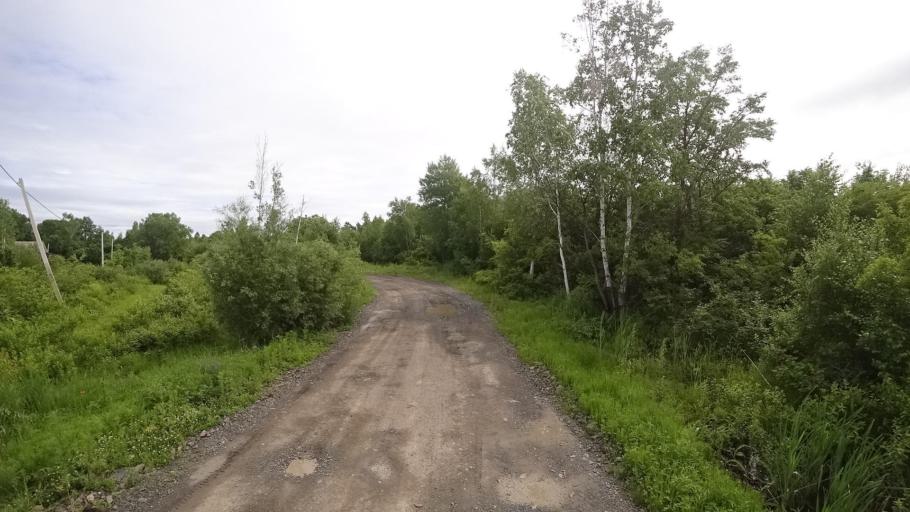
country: RU
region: Khabarovsk Krai
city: Amursk
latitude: 49.8980
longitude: 136.1489
